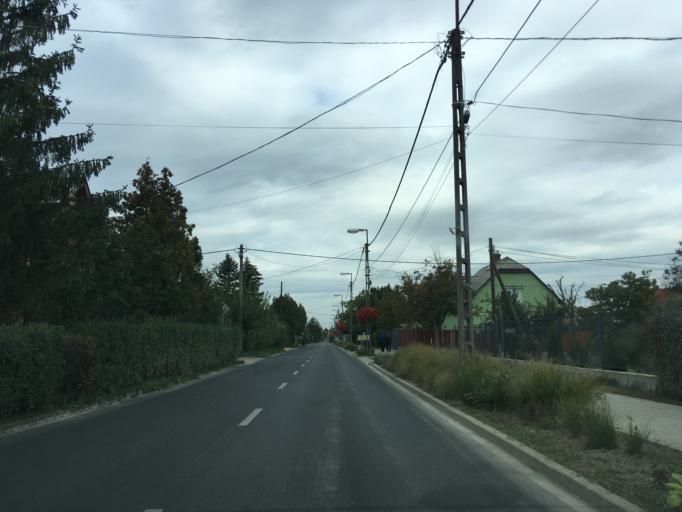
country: HU
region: Pest
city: Szazhalombatta
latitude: 47.3113
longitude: 18.9260
